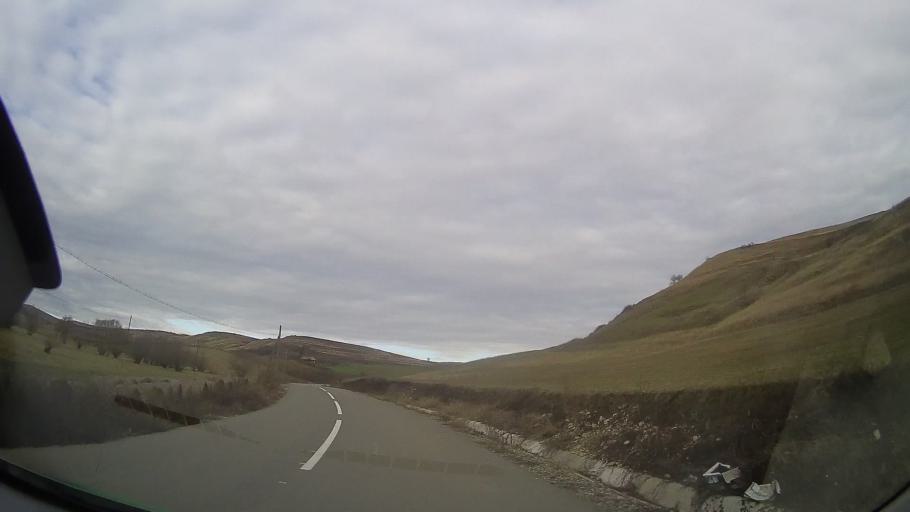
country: RO
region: Bistrita-Nasaud
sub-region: Comuna Silvasu de Campie
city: Silvasu de Campie
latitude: 46.8166
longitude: 24.2974
